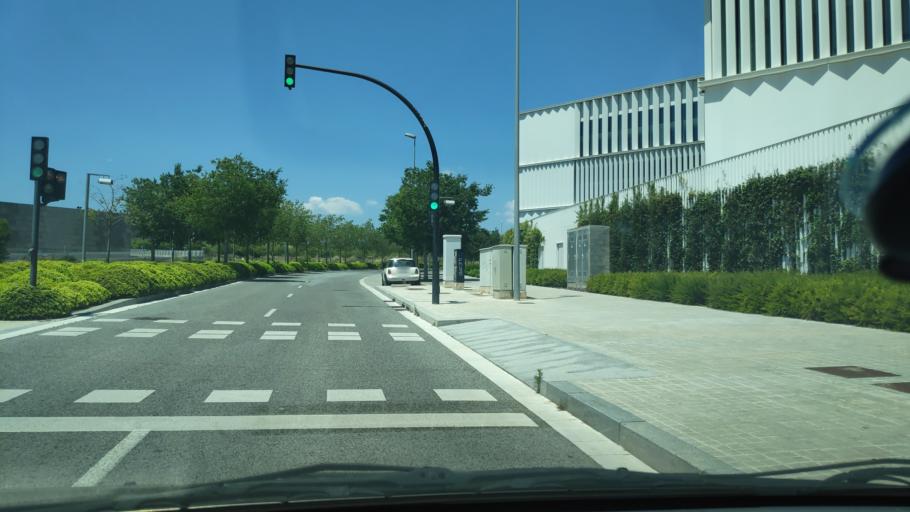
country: ES
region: Catalonia
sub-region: Provincia de Barcelona
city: Barbera del Valles
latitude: 41.4895
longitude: 2.1110
